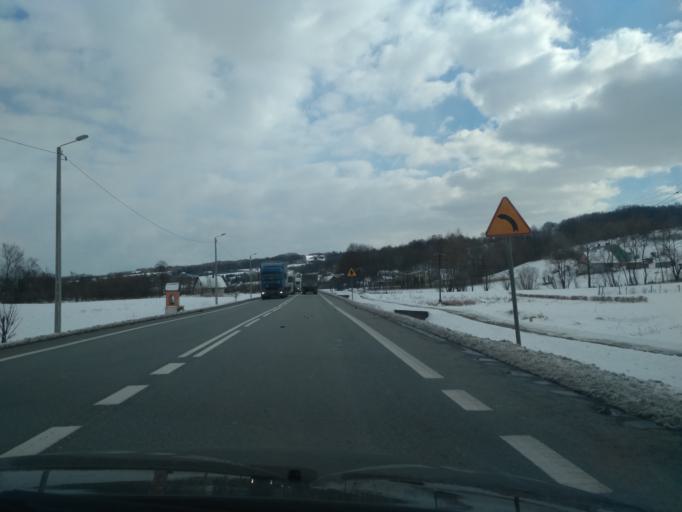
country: PL
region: Subcarpathian Voivodeship
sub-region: Powiat strzyzowski
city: Polomia
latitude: 49.9057
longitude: 21.8664
